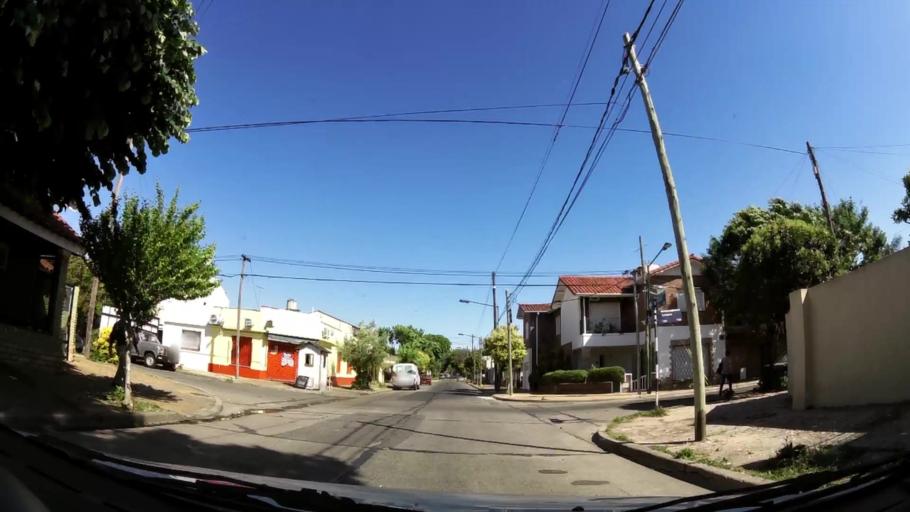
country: AR
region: Buenos Aires
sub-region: Partido de San Isidro
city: San Isidro
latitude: -34.4700
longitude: -58.5288
